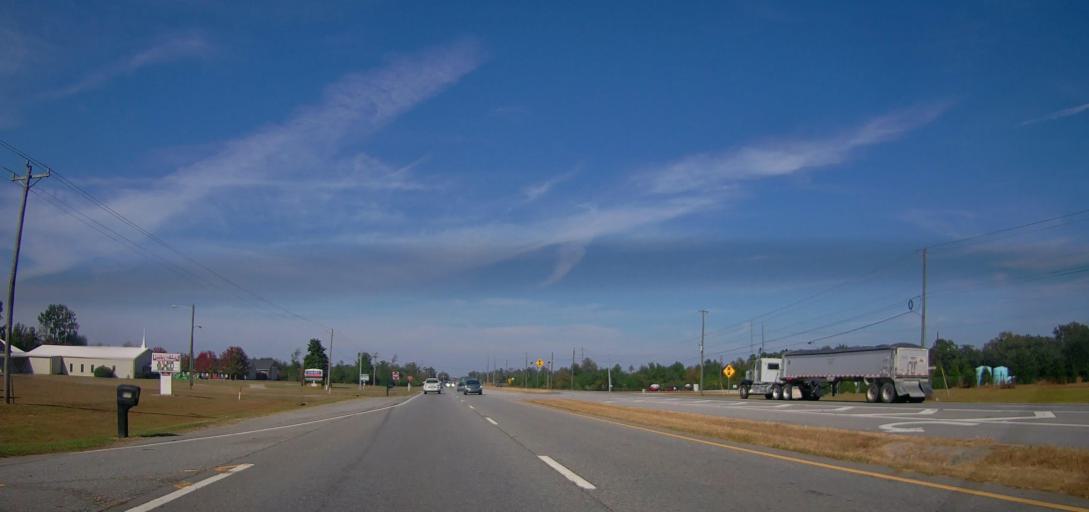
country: US
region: Georgia
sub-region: Dougherty County
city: Putney
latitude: 31.5237
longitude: -84.1157
